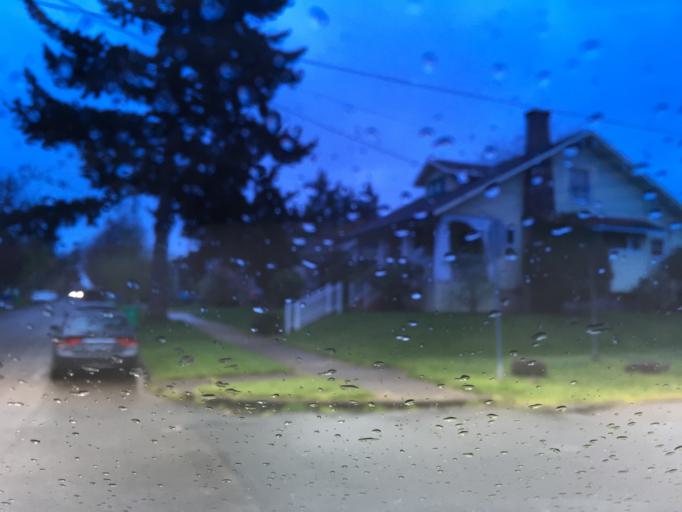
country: US
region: Oregon
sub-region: Multnomah County
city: Lents
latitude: 45.5525
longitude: -122.5932
